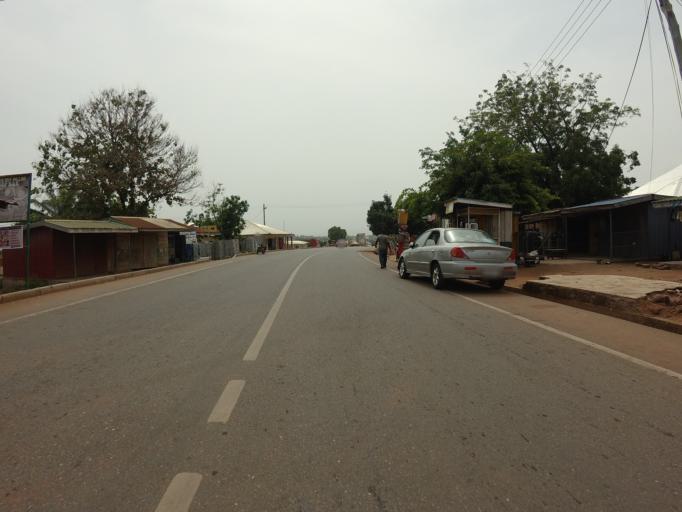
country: GH
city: Akropong
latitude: 6.0866
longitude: -0.0191
